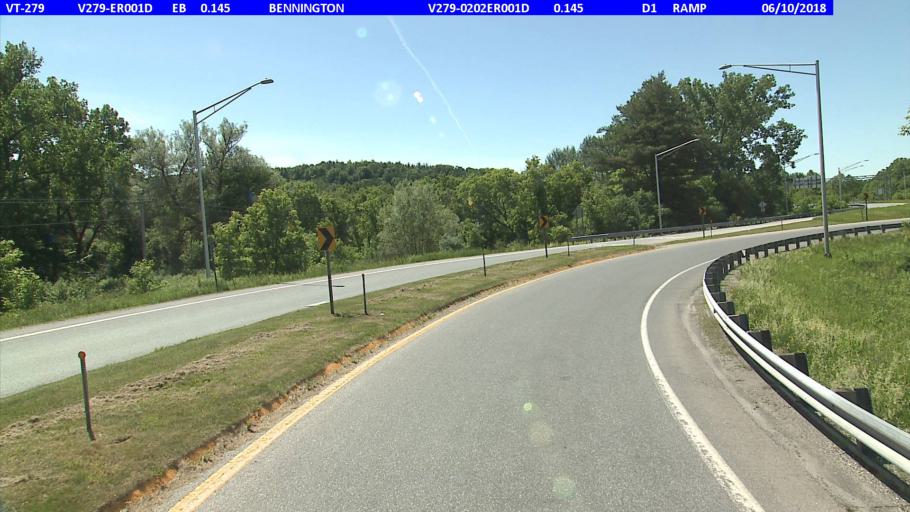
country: US
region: Vermont
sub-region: Bennington County
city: Bennington
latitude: 42.9036
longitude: -73.2196
